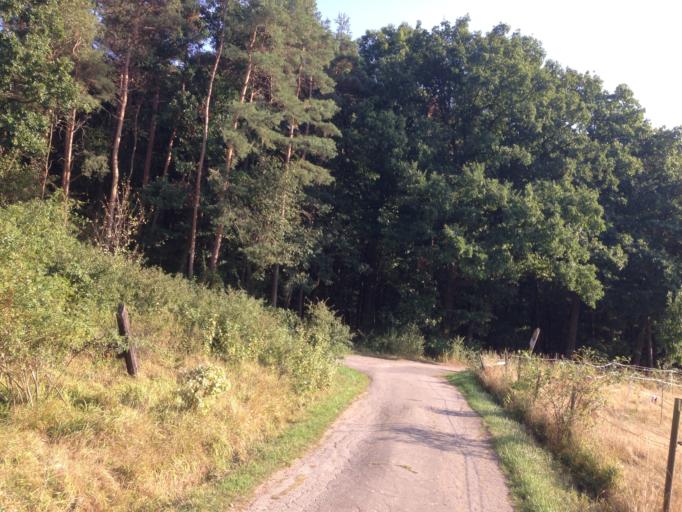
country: DE
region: Hesse
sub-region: Regierungsbezirk Giessen
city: Heuchelheim
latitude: 50.5574
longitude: 8.6557
